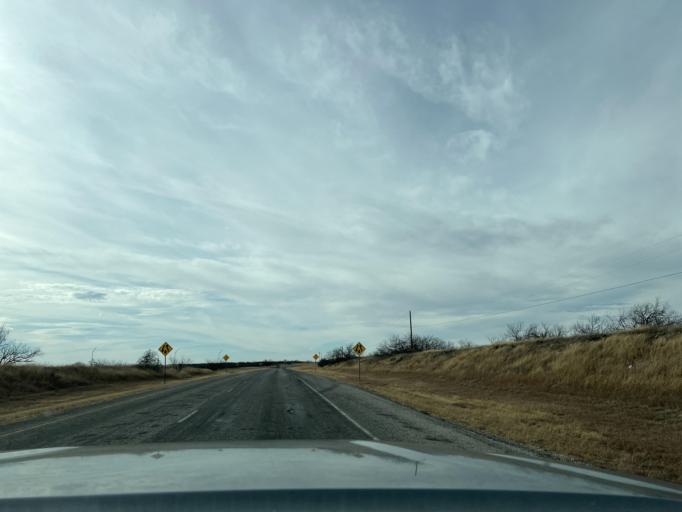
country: US
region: Texas
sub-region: Shackelford County
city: Albany
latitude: 32.7076
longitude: -99.4245
